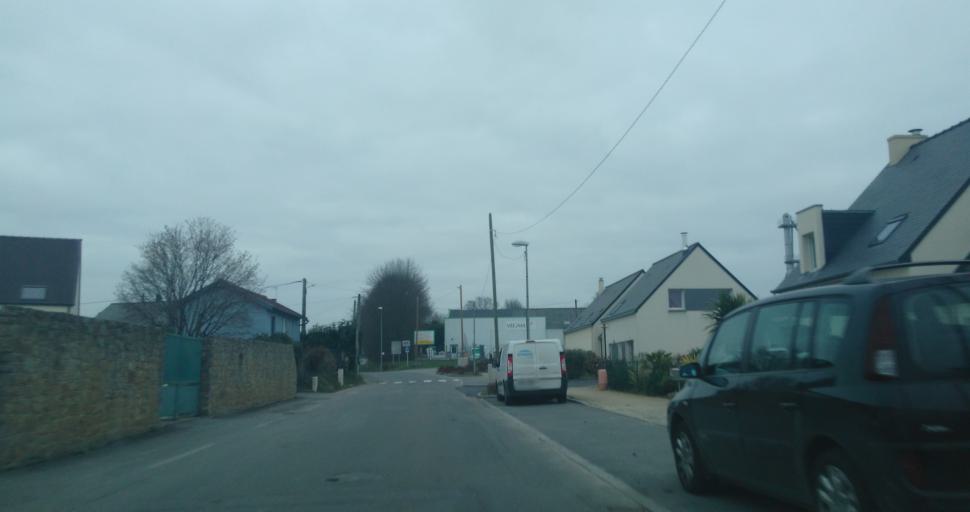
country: FR
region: Brittany
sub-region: Departement d'Ille-et-Vilaine
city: Romille
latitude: 48.2185
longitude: -1.8917
